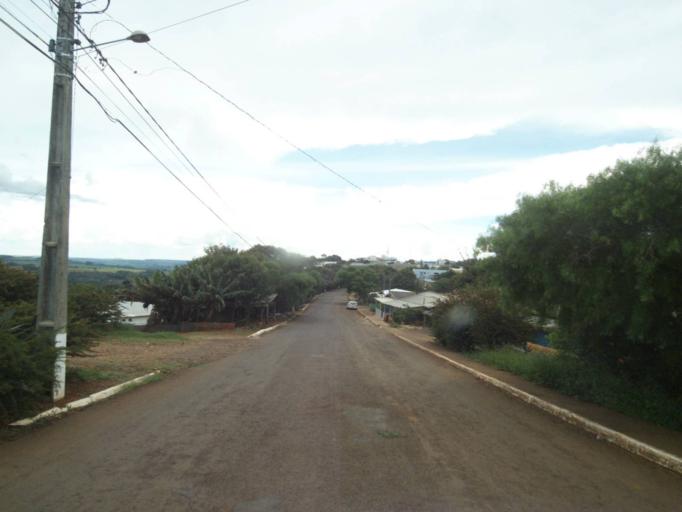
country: BR
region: Parana
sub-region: Guaraniacu
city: Guaraniacu
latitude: -25.1045
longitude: -52.8585
